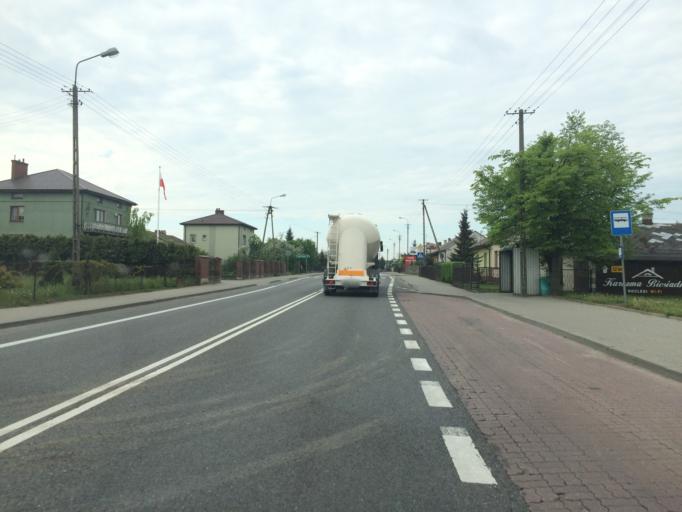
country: PL
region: Masovian Voivodeship
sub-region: Powiat mlawski
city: Wisniewo
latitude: 53.0658
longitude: 20.3485
